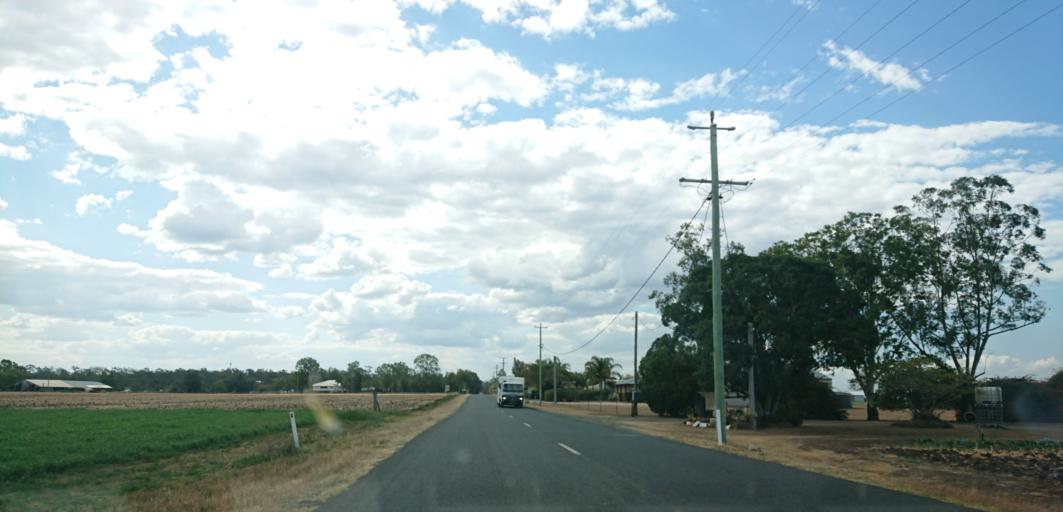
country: AU
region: Queensland
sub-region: Lockyer Valley
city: Gatton
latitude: -27.6128
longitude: 152.2087
